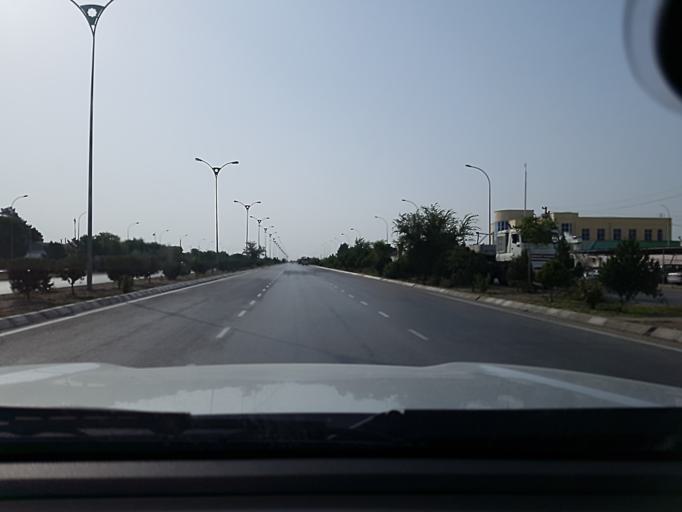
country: TM
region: Balkan
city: Balkanabat
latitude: 39.4992
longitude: 54.3676
